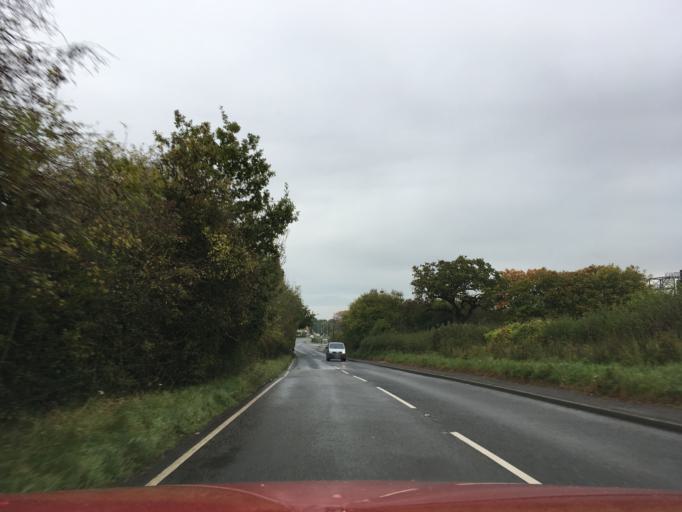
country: GB
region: Wales
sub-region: Monmouthshire
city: Magor
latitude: 51.5878
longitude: -2.8476
